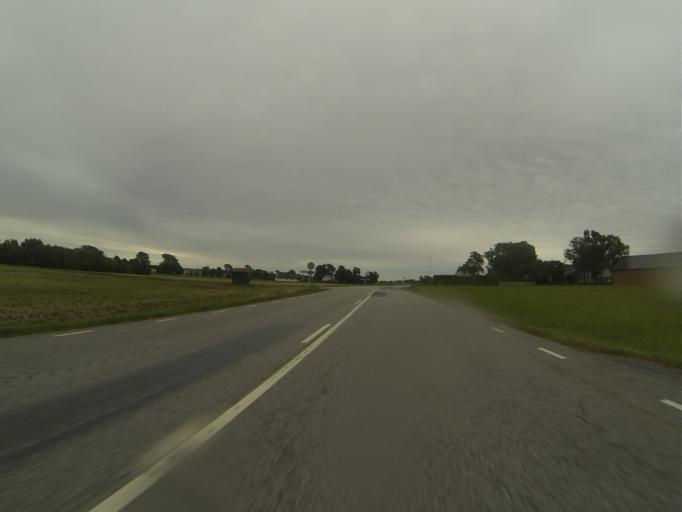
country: SE
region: Skane
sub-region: Svedala Kommun
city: Klagerup
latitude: 55.6341
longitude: 13.2861
